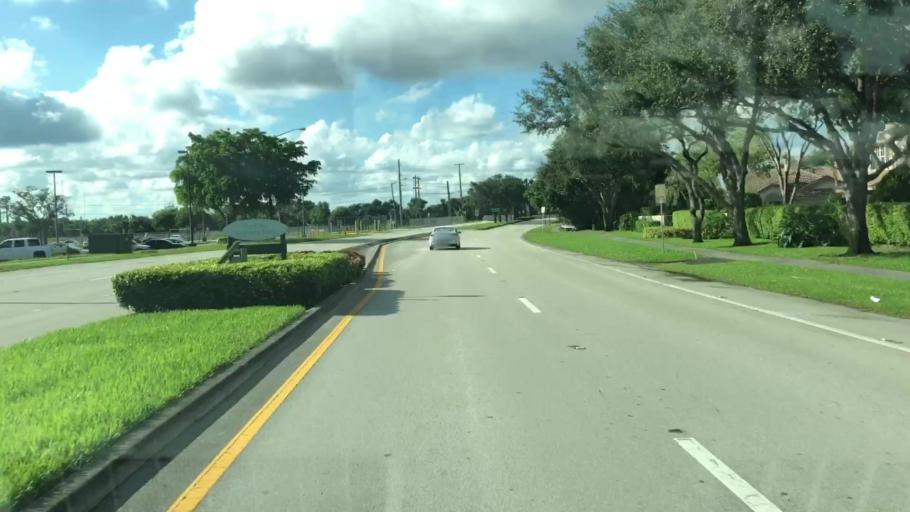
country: US
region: Florida
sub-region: Broward County
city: Tamarac
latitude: 26.2321
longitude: -80.2701
